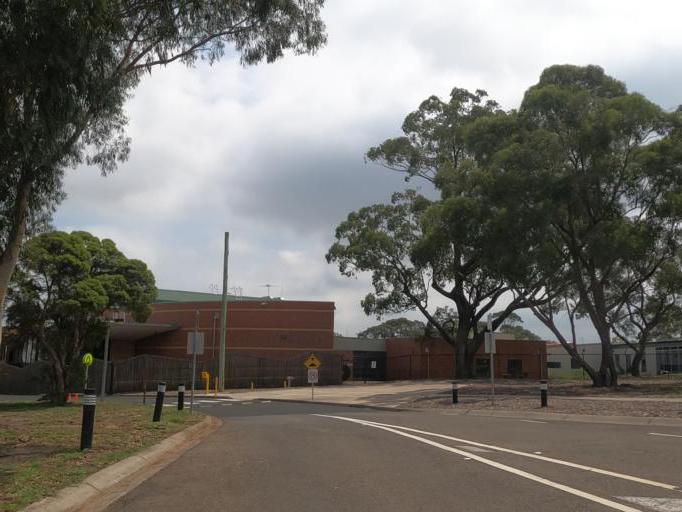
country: AU
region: Victoria
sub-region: Hume
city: Attwood
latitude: -37.6640
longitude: 144.8844
